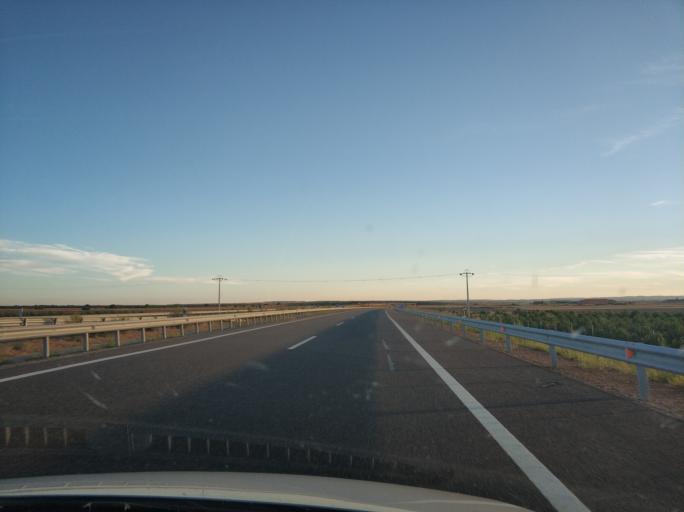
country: ES
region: Castille and Leon
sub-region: Provincia de Zamora
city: Barcial del Barco
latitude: 41.9330
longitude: -5.6482
